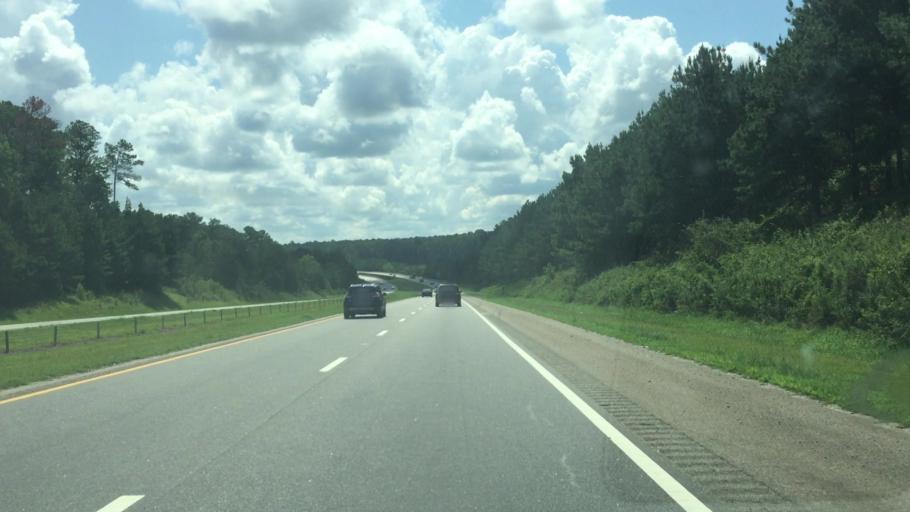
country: US
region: North Carolina
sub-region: Richmond County
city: Cordova
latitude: 34.9255
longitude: -79.8193
